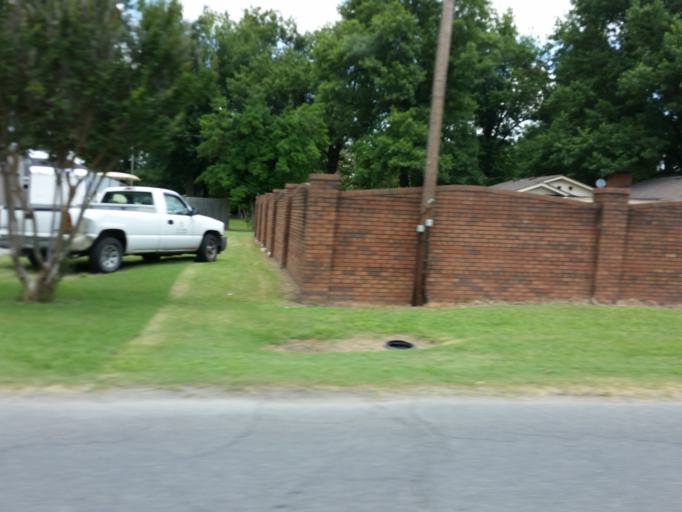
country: US
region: Tennessee
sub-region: Lake County
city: Tiptonville
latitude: 36.3737
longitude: -89.4742
